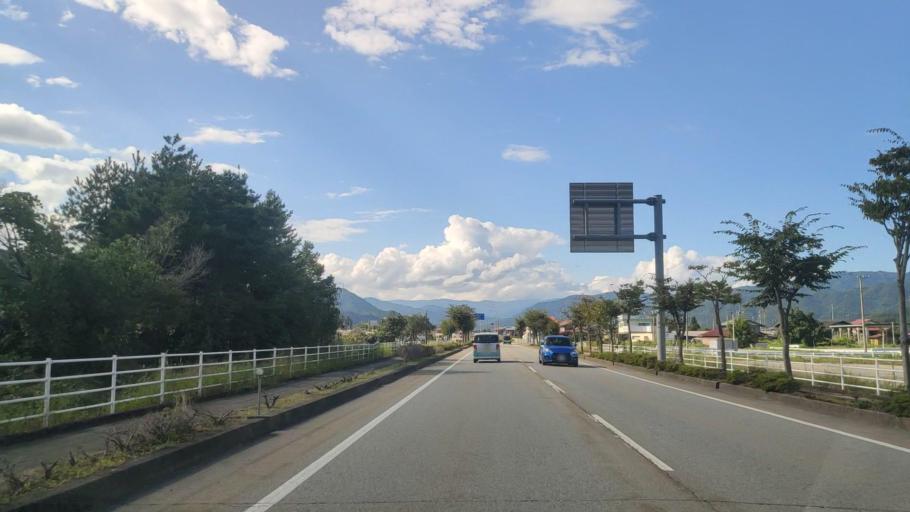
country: JP
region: Gifu
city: Takayama
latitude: 36.2143
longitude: 137.2057
